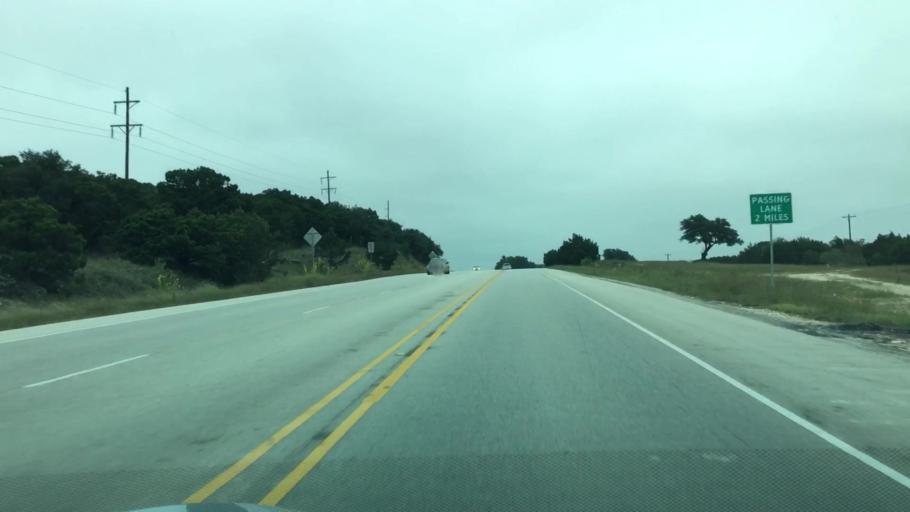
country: US
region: Texas
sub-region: Blanco County
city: Blanco
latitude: 29.9789
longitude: -98.4098
